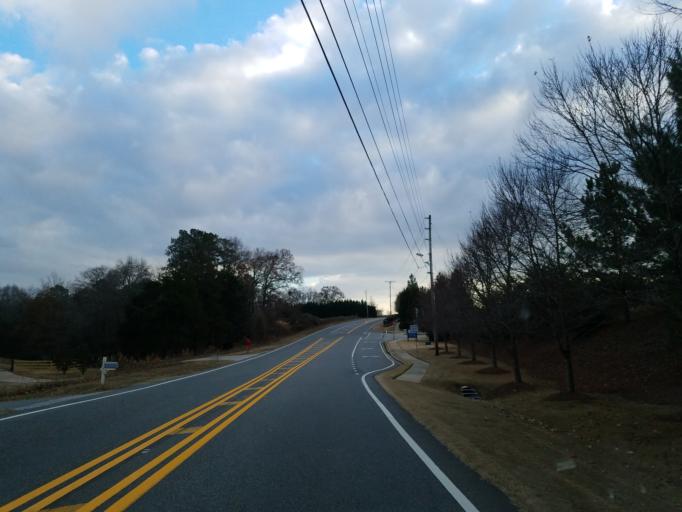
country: US
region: Georgia
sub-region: Forsyth County
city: Cumming
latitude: 34.3050
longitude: -84.0807
